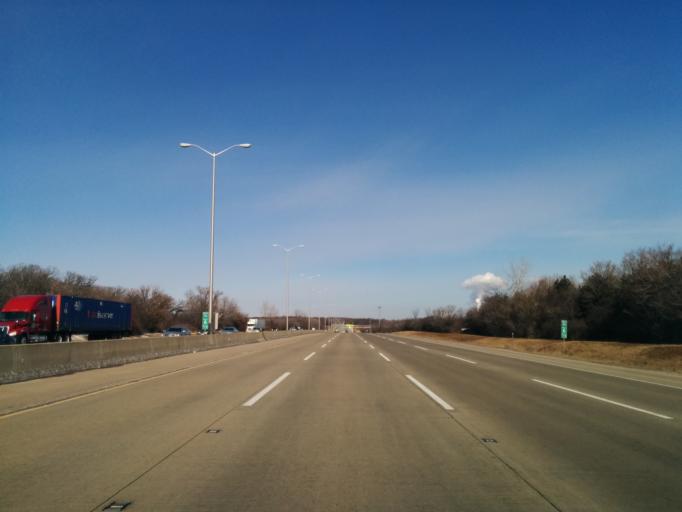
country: US
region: Illinois
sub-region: Lake County
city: Wadsworth
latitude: 42.4084
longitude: -87.9481
